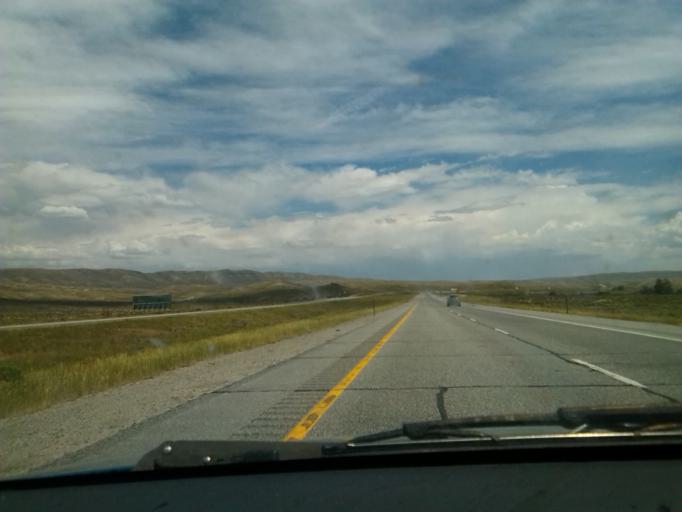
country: US
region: Wyoming
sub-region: Carbon County
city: Saratoga
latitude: 41.7426
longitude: -106.7815
